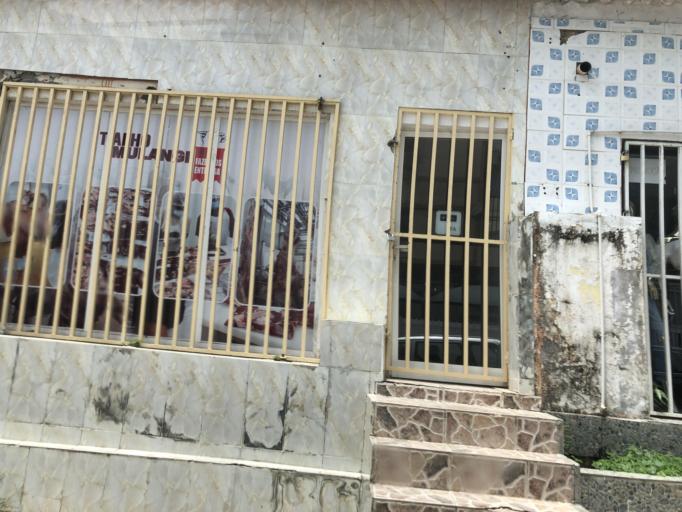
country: AO
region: Luanda
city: Luanda
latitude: -8.8223
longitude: 13.2306
